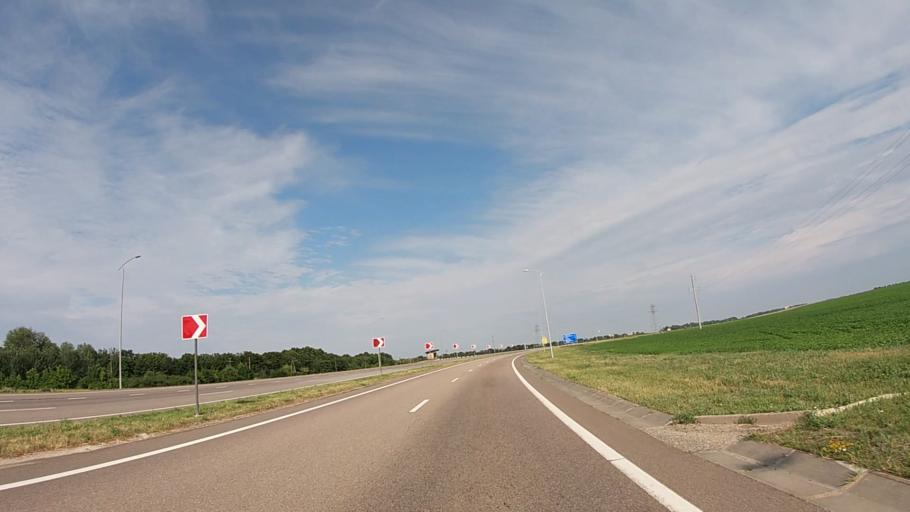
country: RU
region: Belgorod
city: Rakitnoye
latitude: 50.7903
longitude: 35.8715
